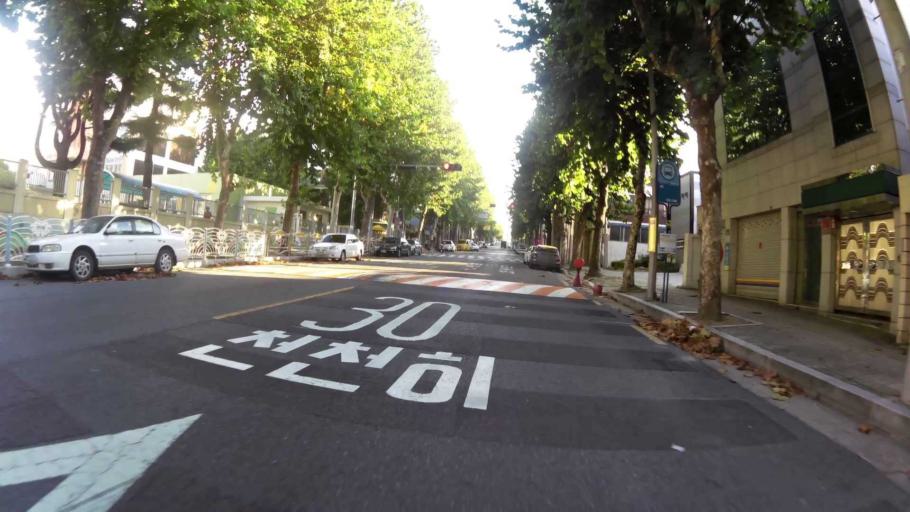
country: KR
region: Daegu
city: Daegu
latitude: 35.8650
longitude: 128.6391
